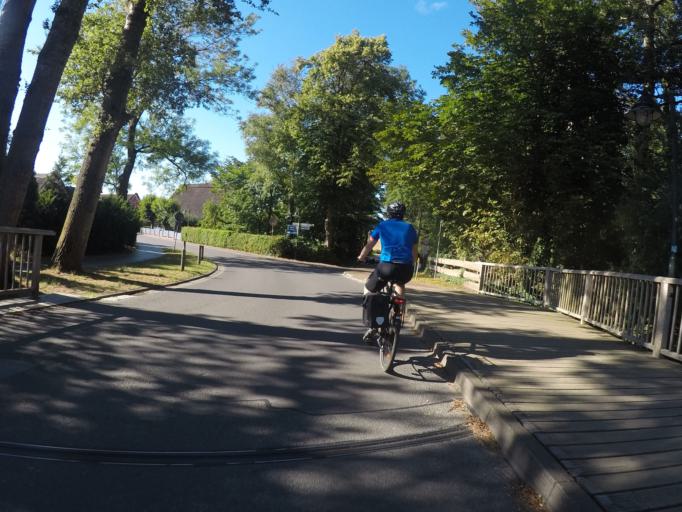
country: DE
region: Lower Saxony
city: Otterndorf
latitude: 53.8224
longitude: 8.8961
